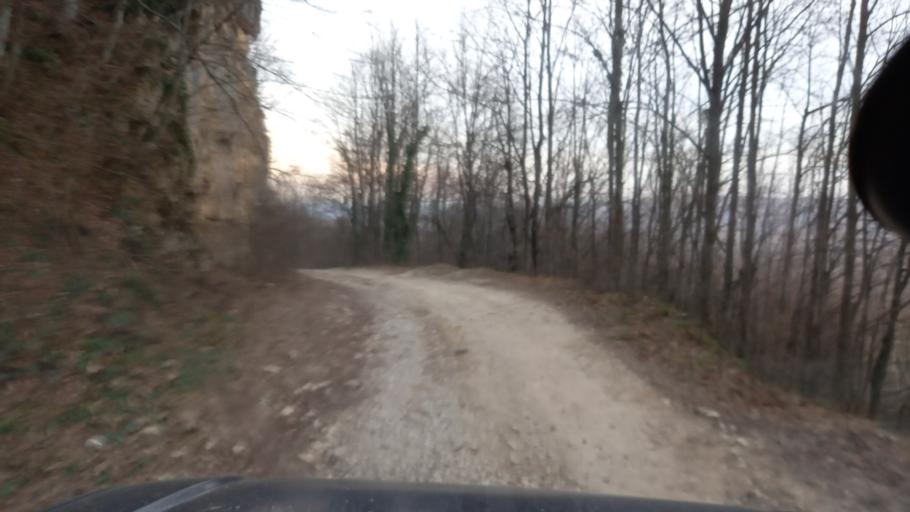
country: RU
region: Krasnodarskiy
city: Neftegorsk
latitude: 44.2202
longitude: 39.8978
